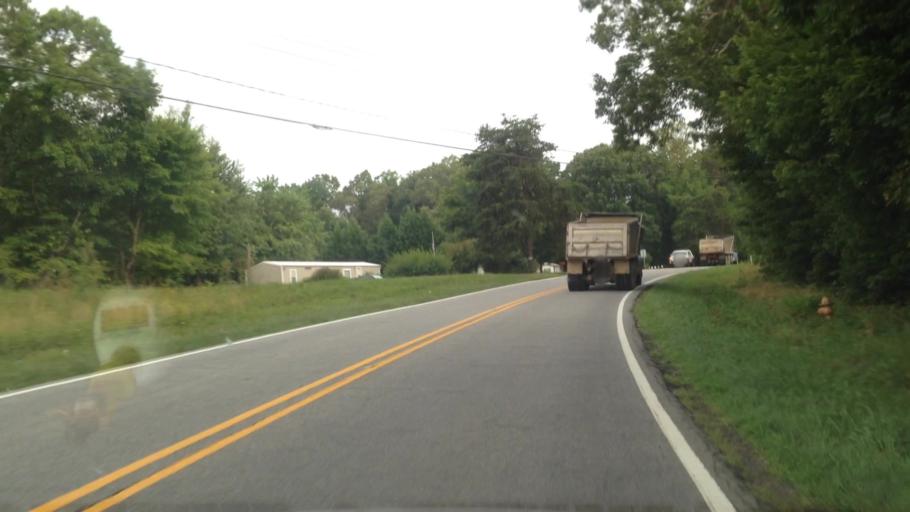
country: US
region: North Carolina
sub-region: Forsyth County
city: Walkertown
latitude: 36.1855
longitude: -80.2083
